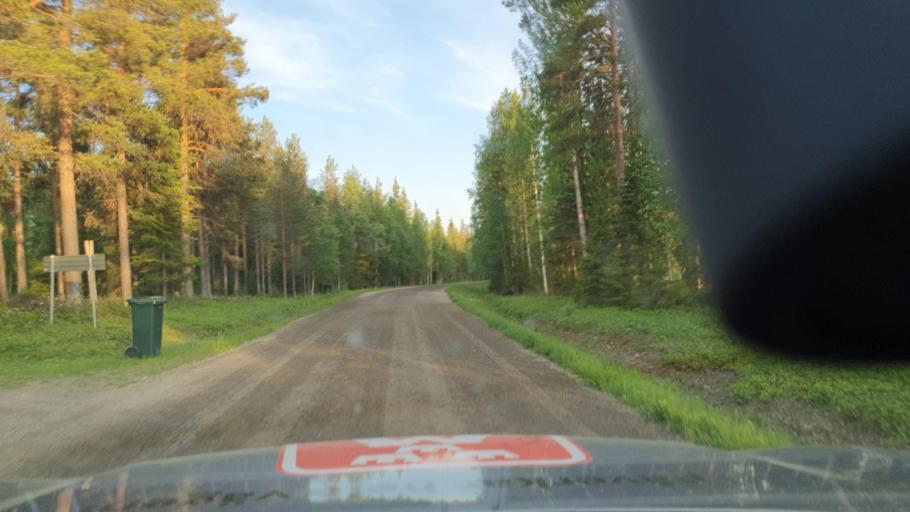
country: SE
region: Norrbotten
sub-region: Bodens Kommun
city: Boden
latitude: 66.1915
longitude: 21.5008
